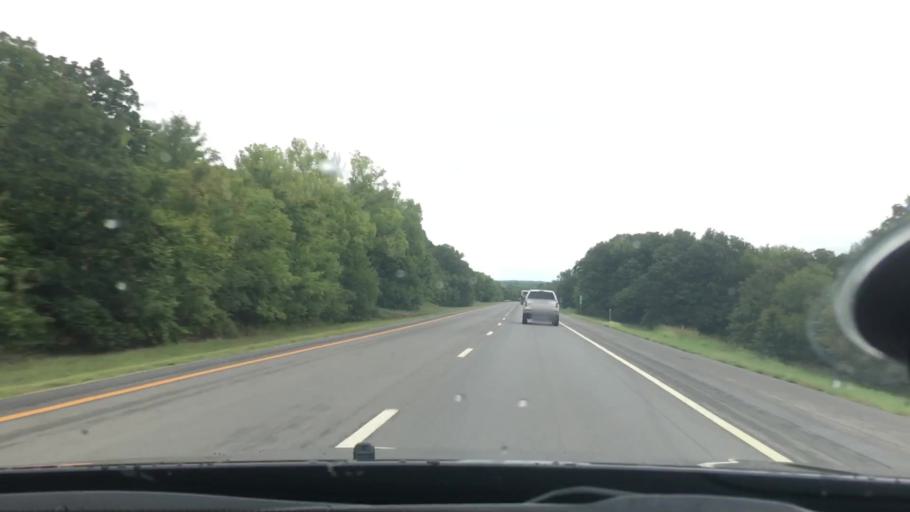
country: US
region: Oklahoma
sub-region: Okmulgee County
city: Morris
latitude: 35.4439
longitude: -95.7727
